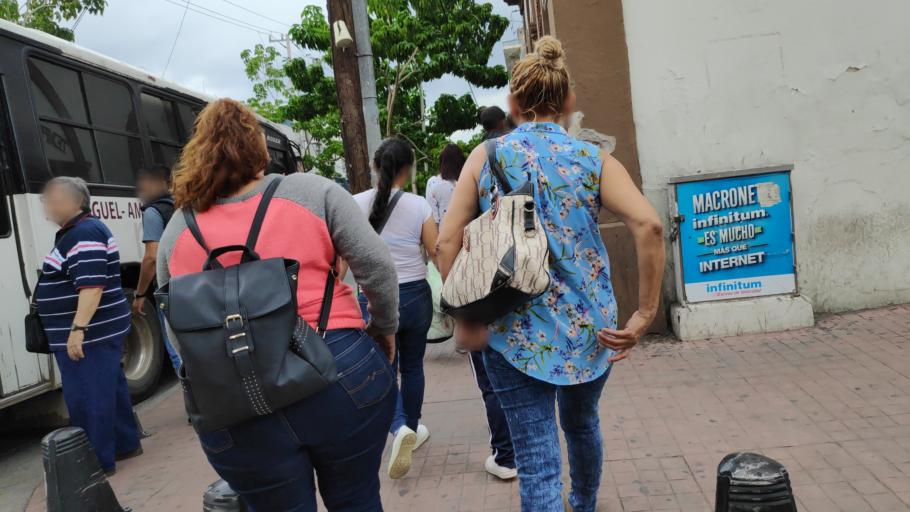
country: MX
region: Sinaloa
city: Culiacan
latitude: 24.8065
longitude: -107.3954
